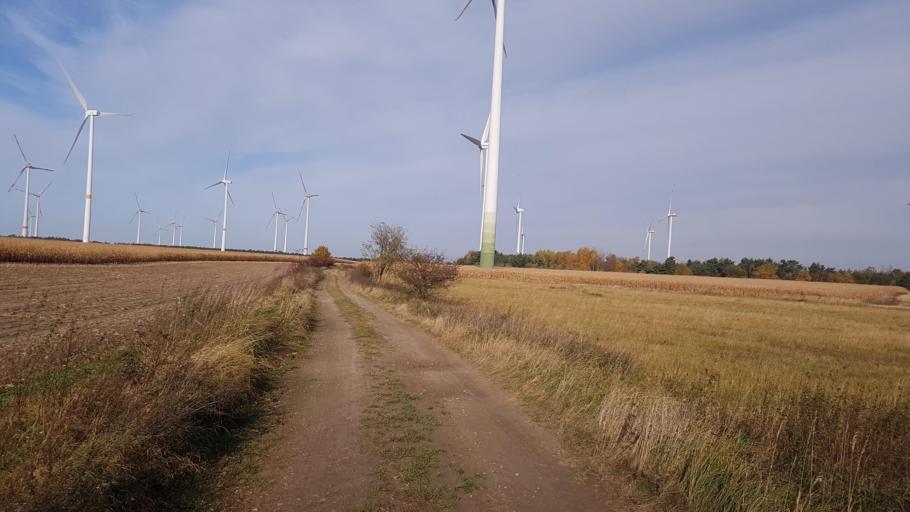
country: DE
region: Brandenburg
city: Treuenbrietzen
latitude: 52.0049
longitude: 12.8835
